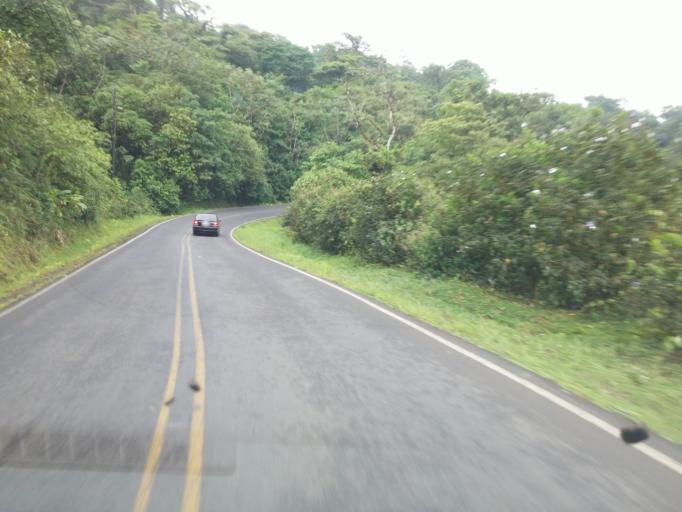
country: CR
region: Alajuela
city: San Ramon
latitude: 10.1967
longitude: -84.5184
